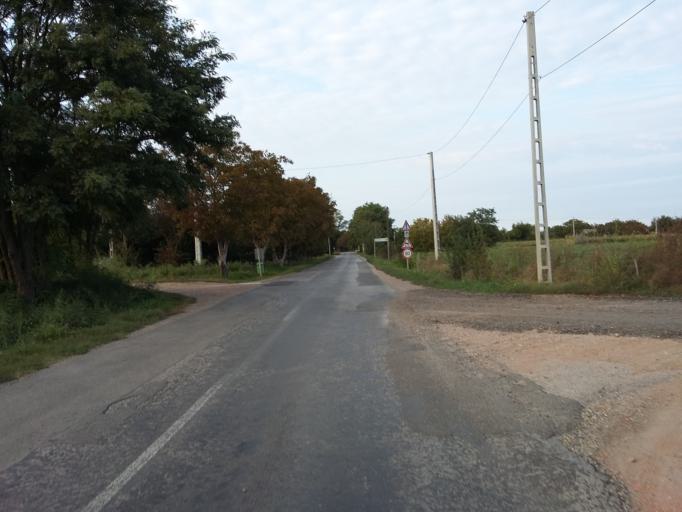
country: HU
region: Csongrad
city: Szeged
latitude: 46.2179
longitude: 20.1105
